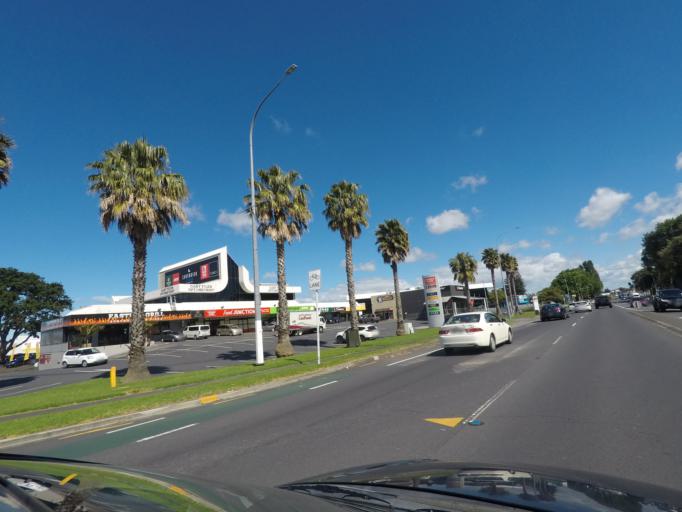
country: NZ
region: Auckland
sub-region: Auckland
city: Manukau City
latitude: -36.9866
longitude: 174.8811
